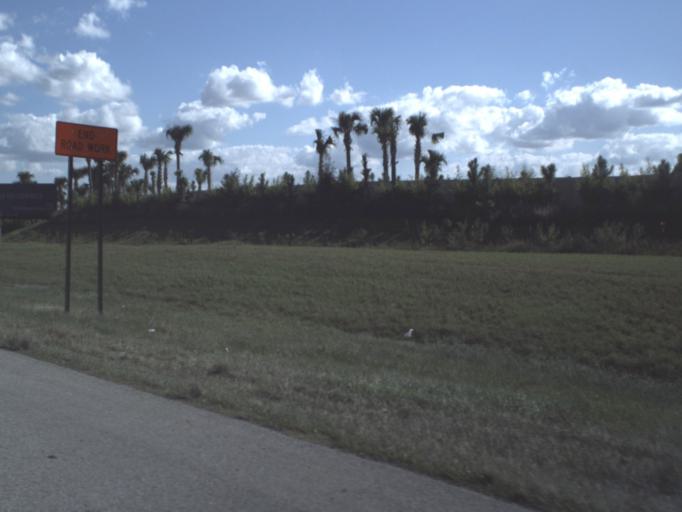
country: US
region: Florida
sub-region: Lake County
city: Montverde
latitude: 28.5865
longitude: -81.7089
